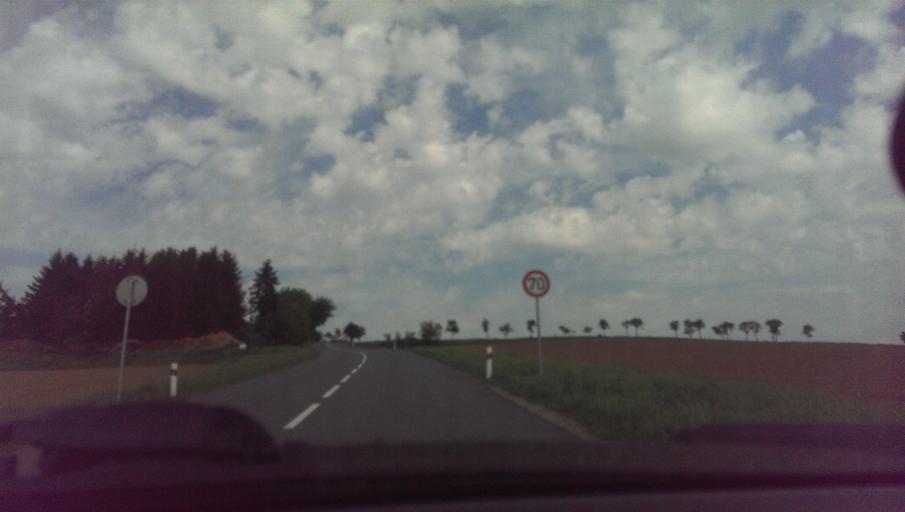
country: CZ
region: Zlin
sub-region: Okres Zlin
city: Otrokovice
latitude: 49.2473
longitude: 17.5435
